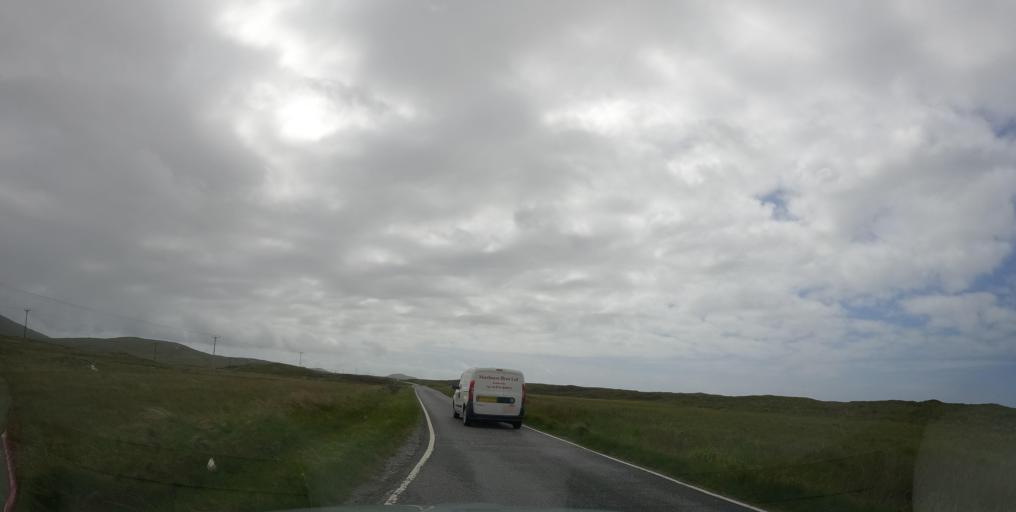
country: GB
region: Scotland
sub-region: Eilean Siar
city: Isle of South Uist
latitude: 57.2786
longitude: -7.3660
